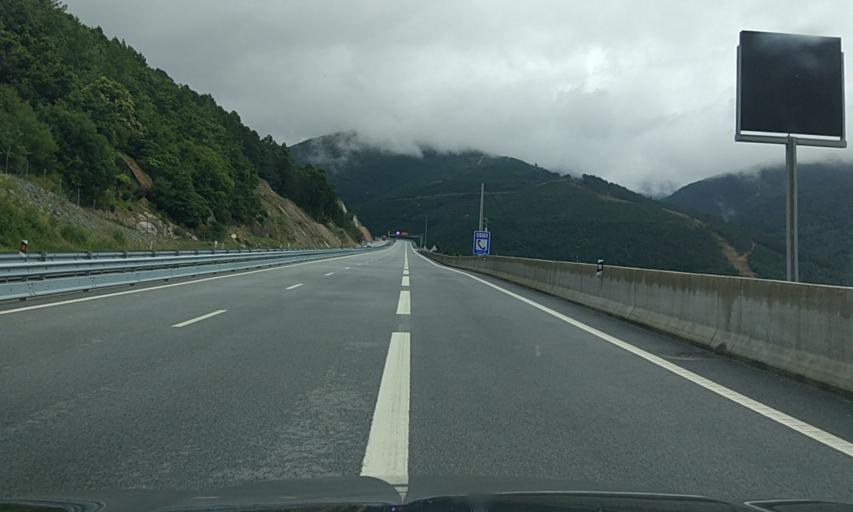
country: PT
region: Porto
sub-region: Baiao
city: Valadares
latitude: 41.2569
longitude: -7.9565
